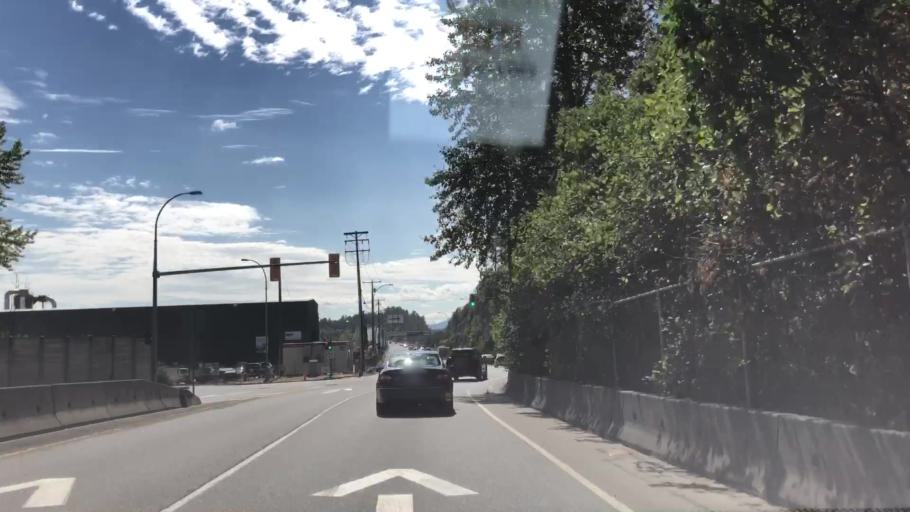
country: CA
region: British Columbia
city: Nanaimo
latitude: 49.1563
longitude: -123.8911
